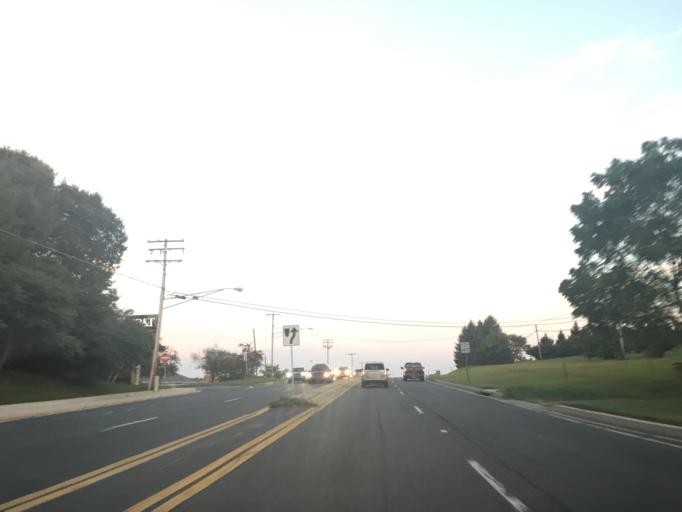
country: US
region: Maryland
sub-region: Harford County
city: Bel Air North
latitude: 39.5621
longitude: -76.3727
